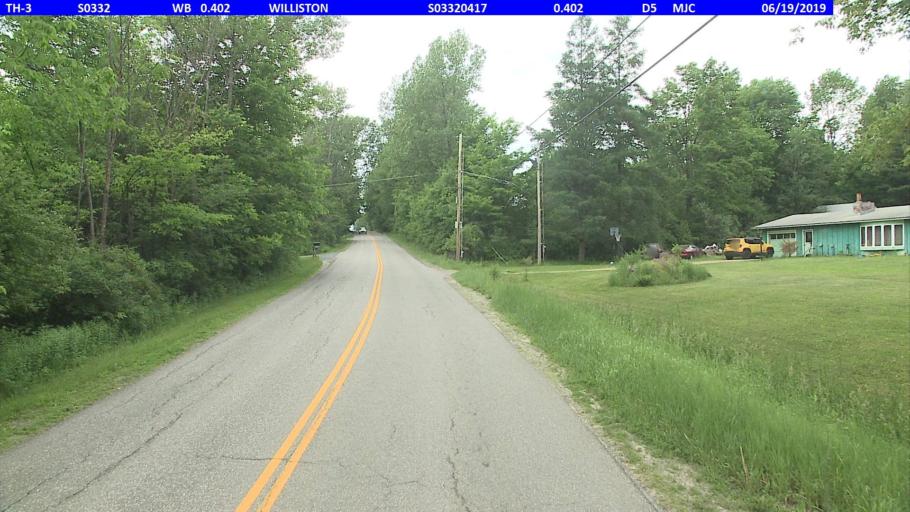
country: US
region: Vermont
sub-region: Chittenden County
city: Williston
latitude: 44.4257
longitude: -73.1140
